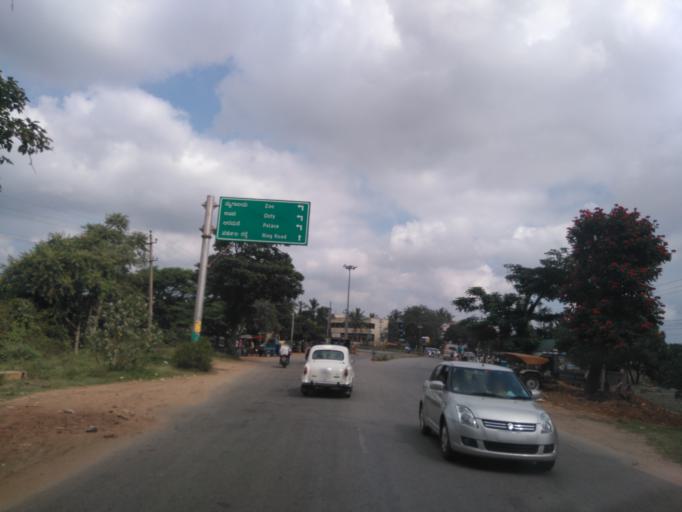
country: IN
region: Karnataka
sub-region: Mysore
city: Mysore
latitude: 12.3015
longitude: 76.6930
